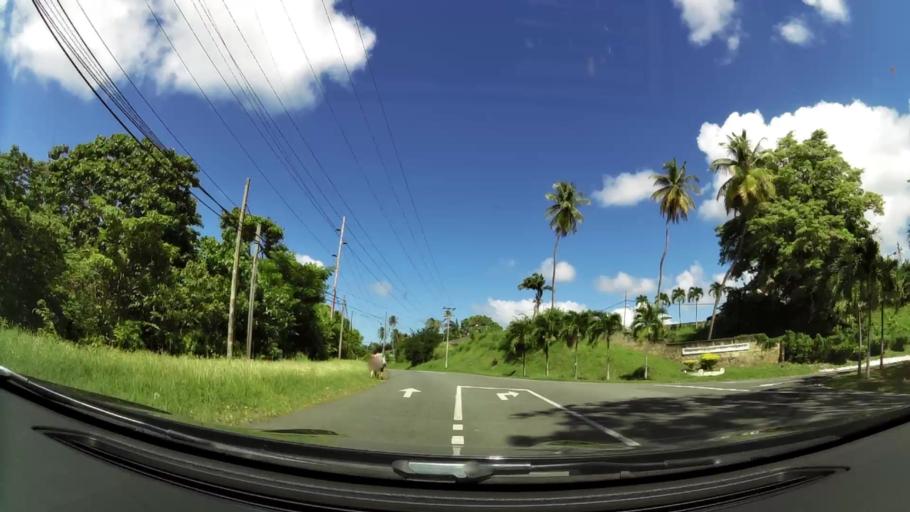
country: TT
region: Tobago
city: Scarborough
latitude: 11.1898
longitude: -60.7955
